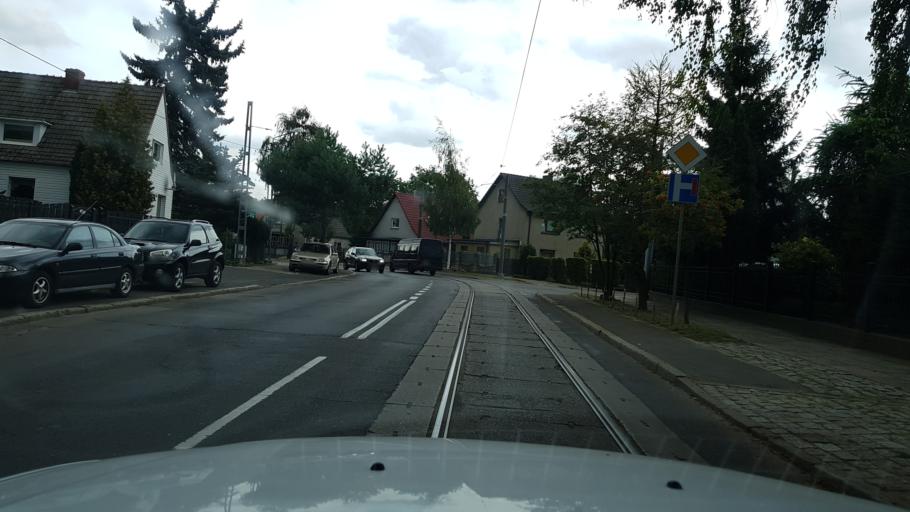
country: PL
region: West Pomeranian Voivodeship
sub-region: Powiat policki
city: Przeclaw
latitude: 53.4210
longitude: 14.4976
